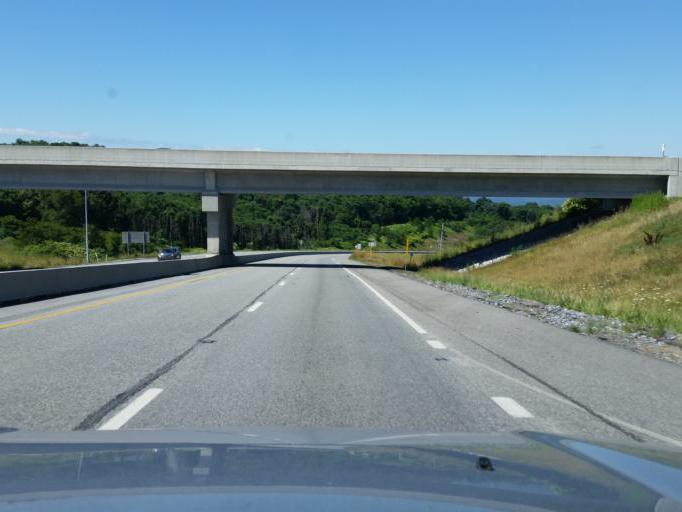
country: US
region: Pennsylvania
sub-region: Cambria County
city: Vinco
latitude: 40.4347
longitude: -78.9112
